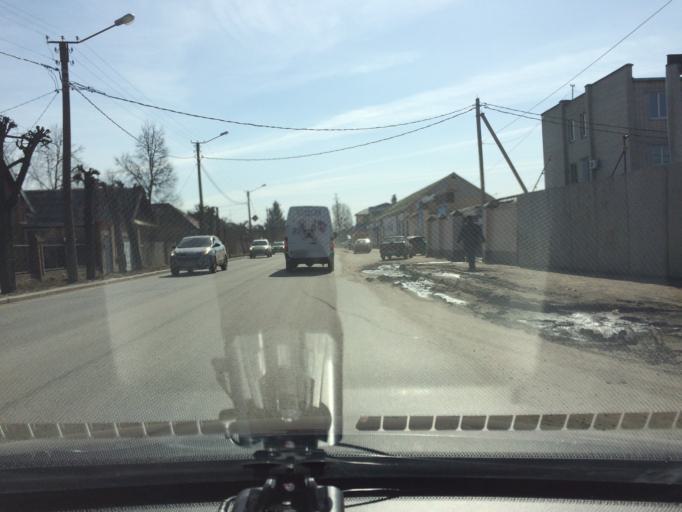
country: RU
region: Mariy-El
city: Yoshkar-Ola
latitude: 56.6484
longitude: 47.9029
